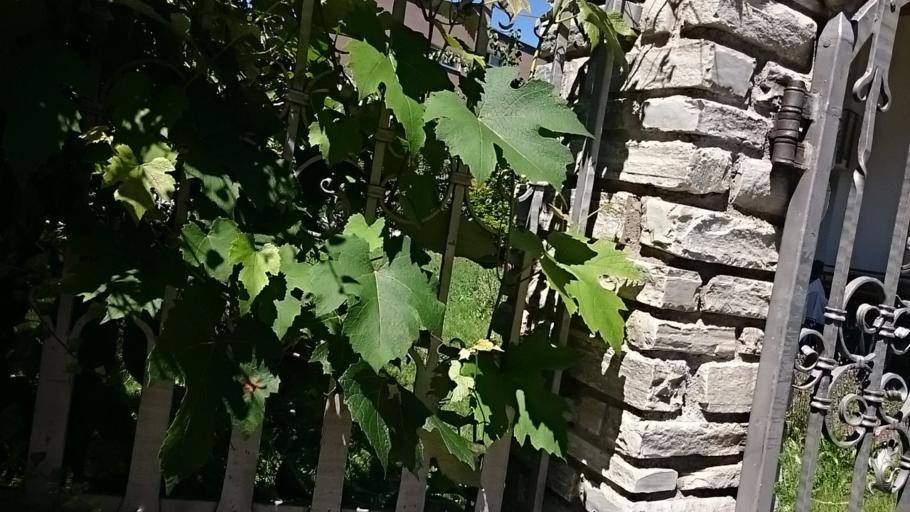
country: IT
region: Trentino-Alto Adige
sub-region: Bolzano
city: Brunico
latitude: 46.7914
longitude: 11.9471
